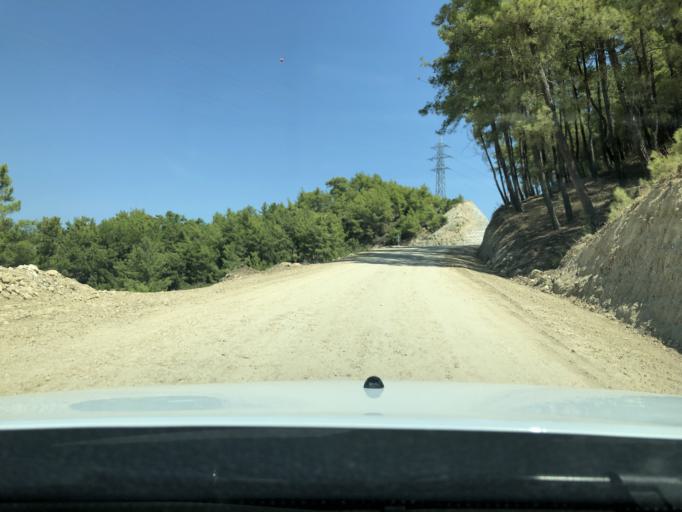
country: TR
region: Antalya
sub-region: Manavgat
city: Manavgat
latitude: 36.8345
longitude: 31.5336
